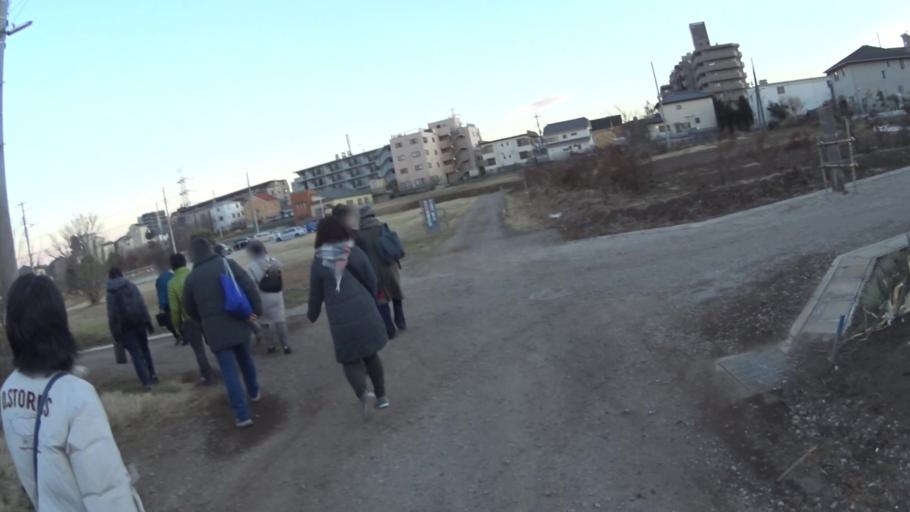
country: JP
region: Saitama
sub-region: Kawaguchi-shi
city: Hatogaya-honcho
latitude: 35.8759
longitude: 139.7393
